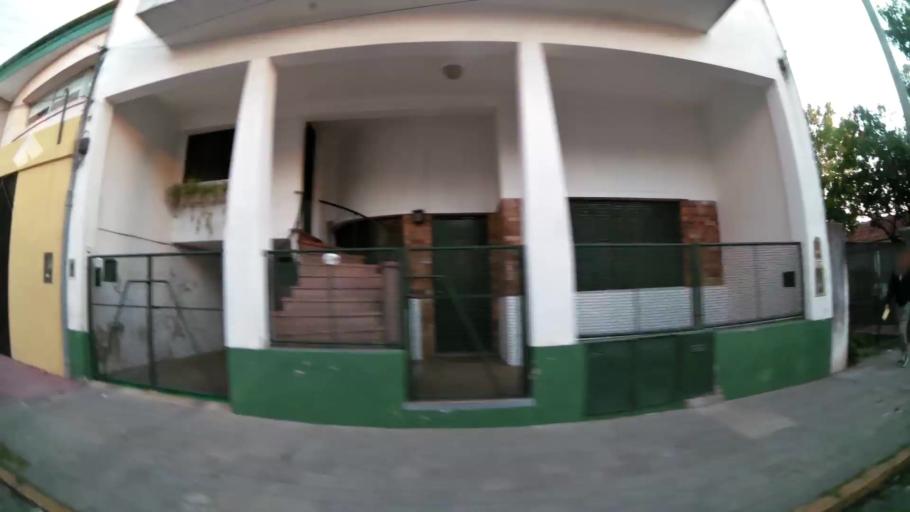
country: AR
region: Buenos Aires
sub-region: Partido de Tigre
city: Tigre
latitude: -34.4412
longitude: -58.5624
